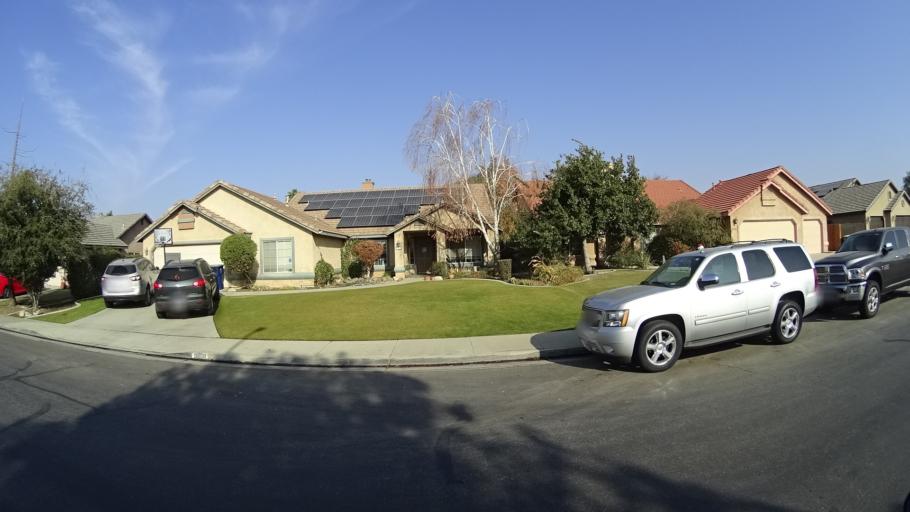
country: US
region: California
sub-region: Kern County
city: Greenacres
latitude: 35.4077
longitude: -119.1120
